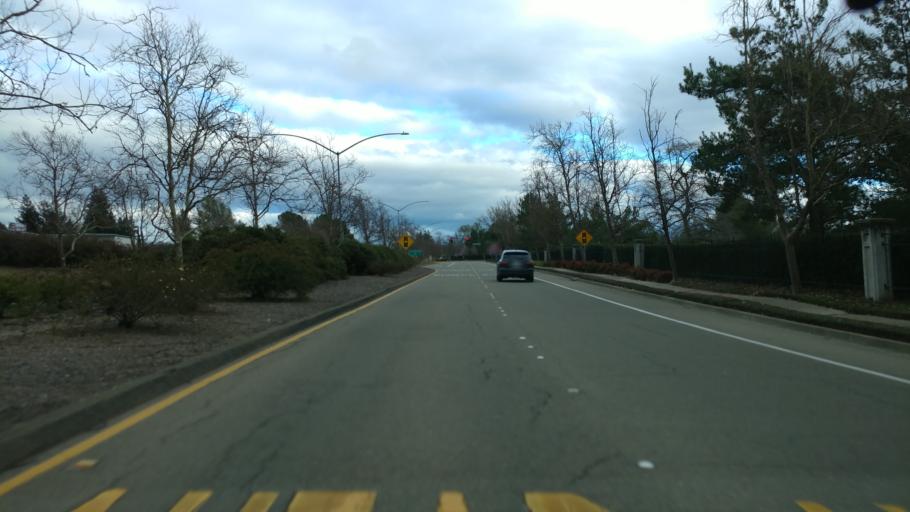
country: US
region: California
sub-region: Contra Costa County
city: San Ramon
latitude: 37.7871
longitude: -121.9446
